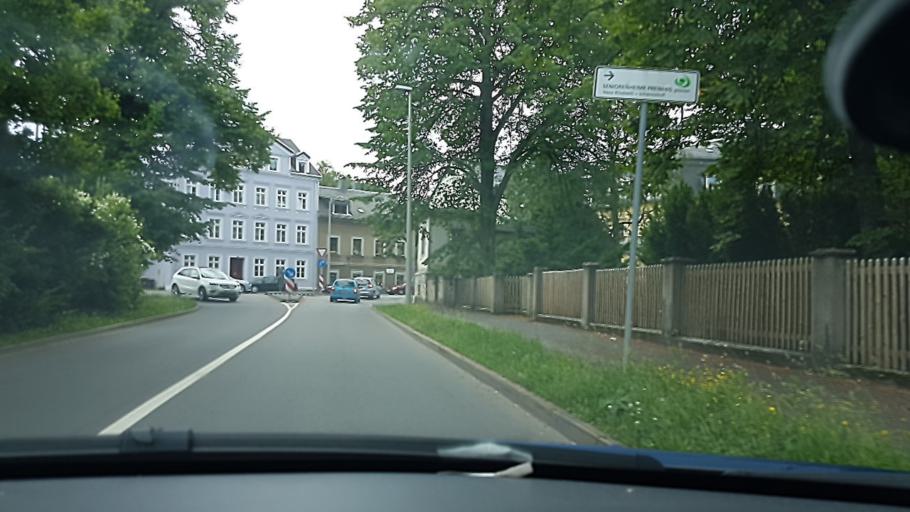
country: DE
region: Saxony
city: Freiberg
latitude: 50.9146
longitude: 13.3371
